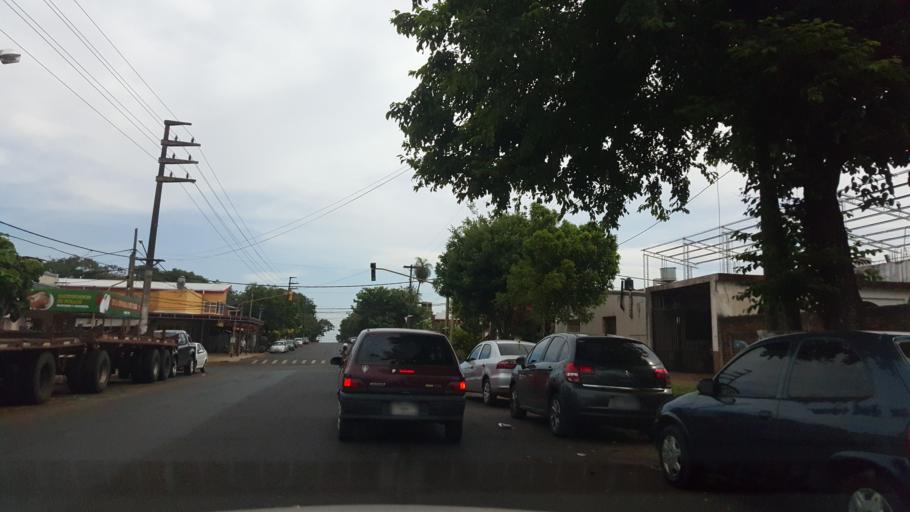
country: AR
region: Misiones
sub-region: Departamento de Capital
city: Posadas
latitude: -27.3636
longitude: -55.9084
